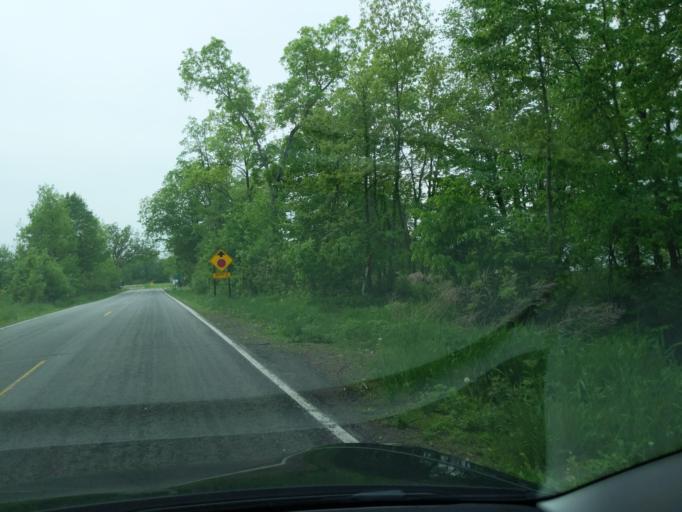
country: US
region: Michigan
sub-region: Ingham County
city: Leslie
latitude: 42.4463
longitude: -84.3535
